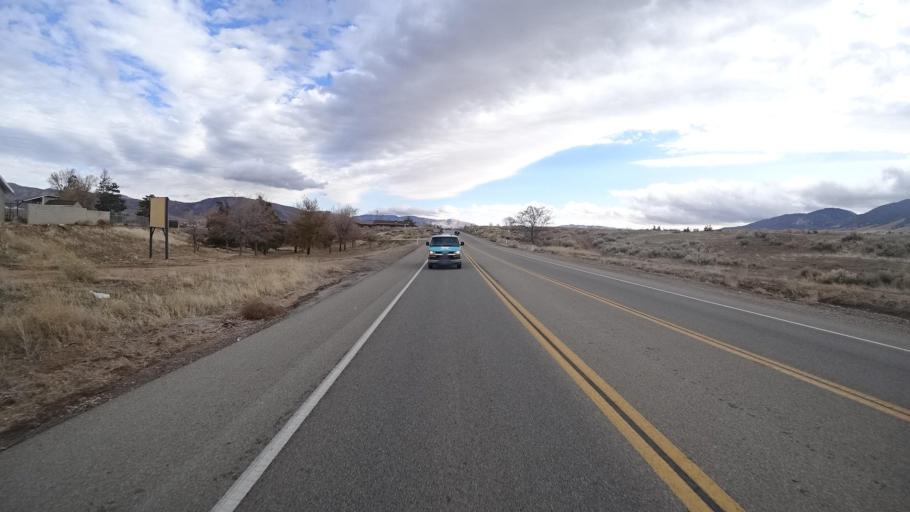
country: US
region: California
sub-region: Kern County
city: Golden Hills
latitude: 35.1243
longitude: -118.4842
